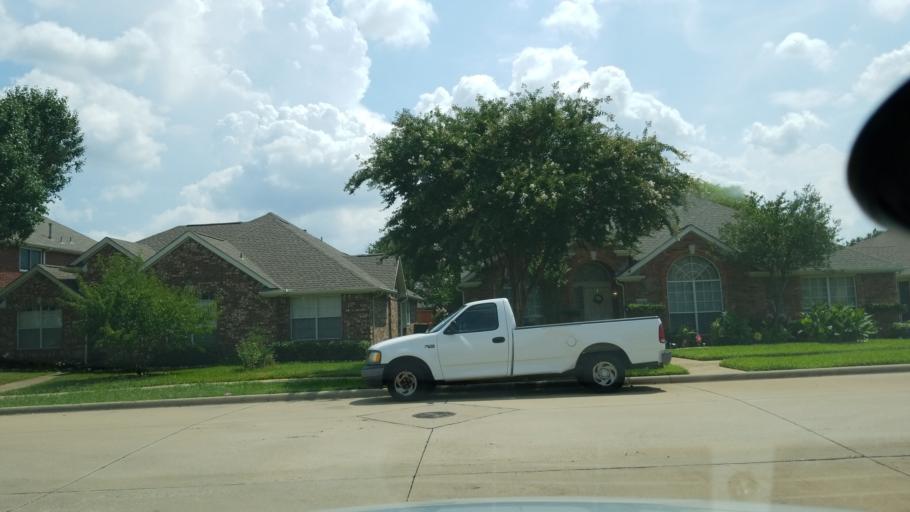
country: US
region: Texas
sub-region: Dallas County
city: Garland
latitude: 32.9289
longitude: -96.6604
